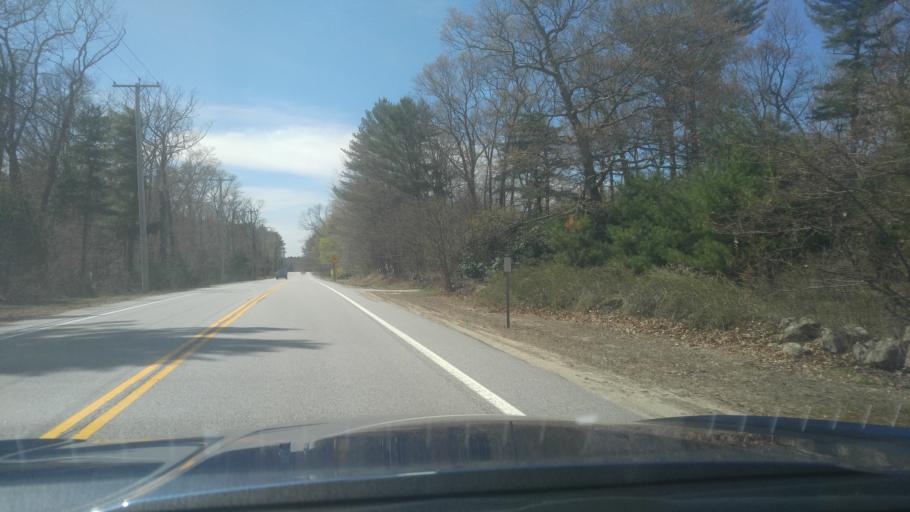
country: US
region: Rhode Island
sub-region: Kent County
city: West Greenwich
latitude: 41.5779
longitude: -71.6685
